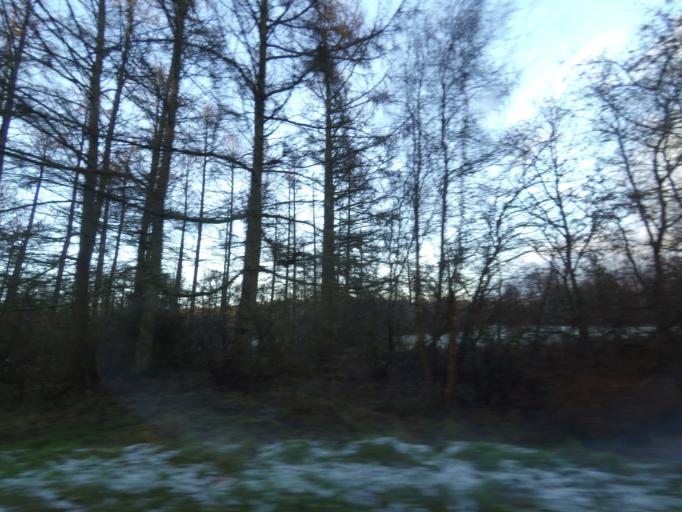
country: DK
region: Central Jutland
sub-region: Ikast-Brande Kommune
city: Brande
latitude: 56.0019
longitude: 9.1787
